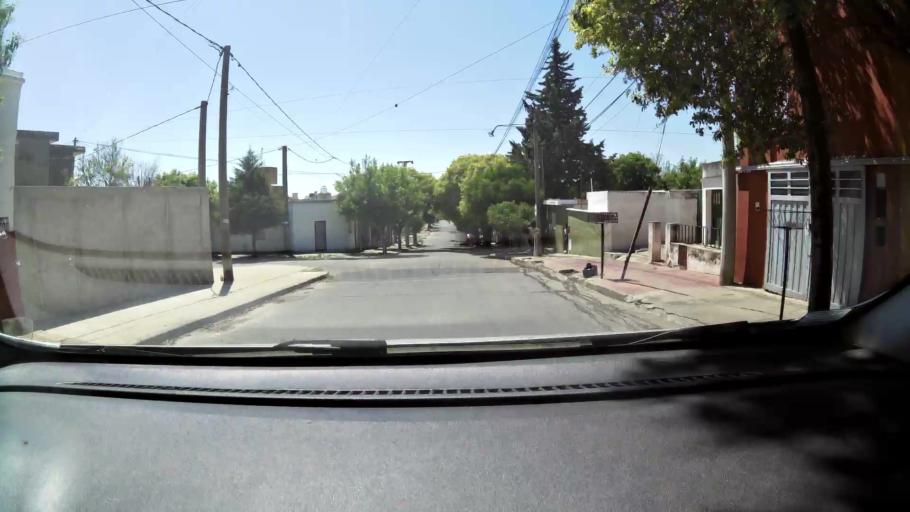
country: AR
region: Cordoba
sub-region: Departamento de Capital
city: Cordoba
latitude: -31.4296
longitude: -64.2049
